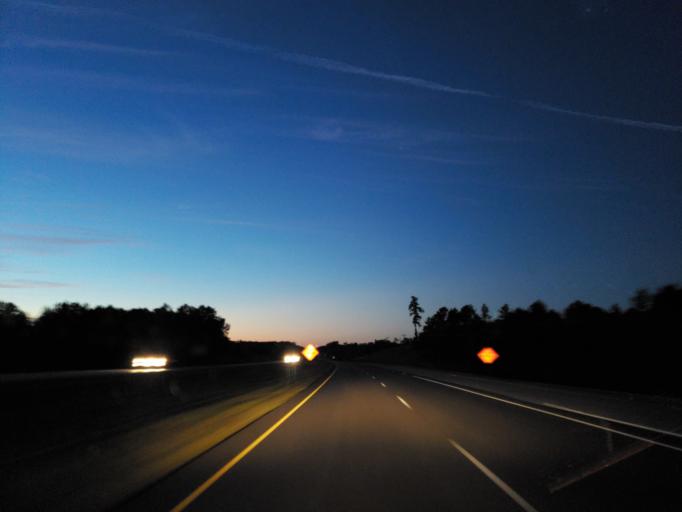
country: US
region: Mississippi
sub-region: Clarke County
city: Quitman
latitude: 32.0641
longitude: -88.6804
